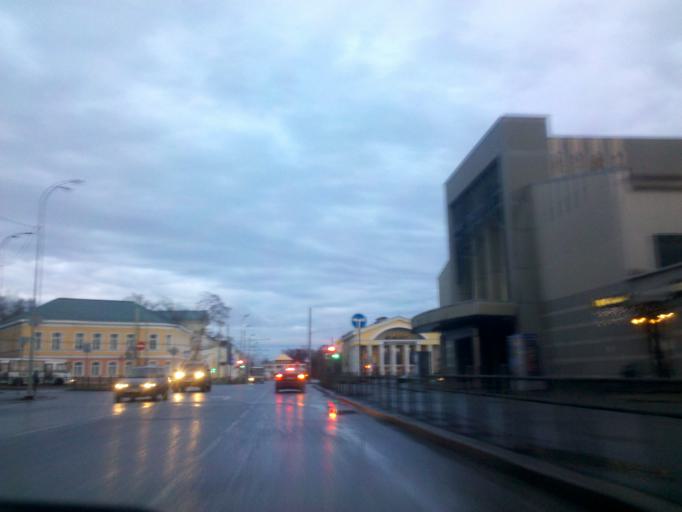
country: RU
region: Republic of Karelia
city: Petrozavodsk
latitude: 61.7879
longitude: 34.3785
